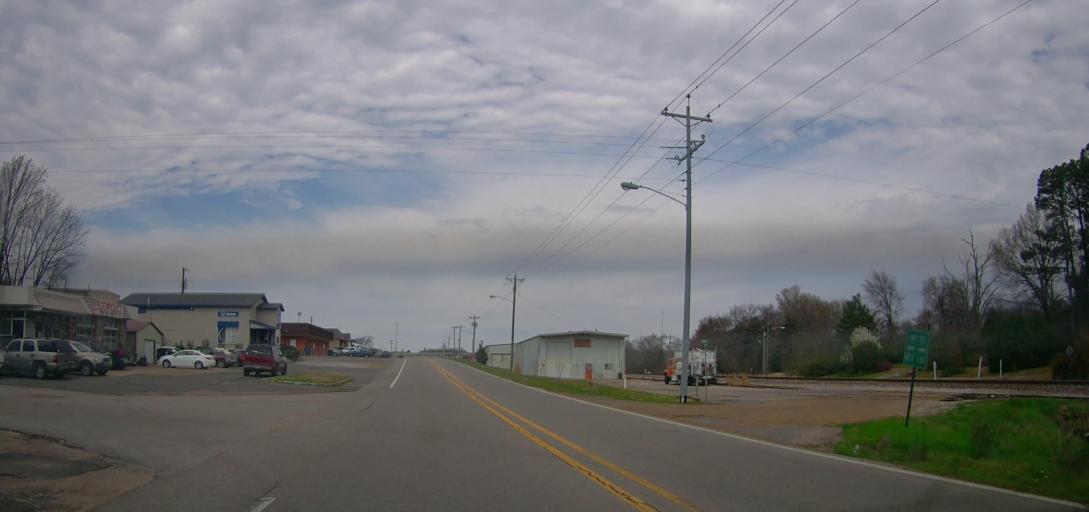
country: US
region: Mississippi
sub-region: De Soto County
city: Olive Branch
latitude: 34.9635
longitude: -89.8269
